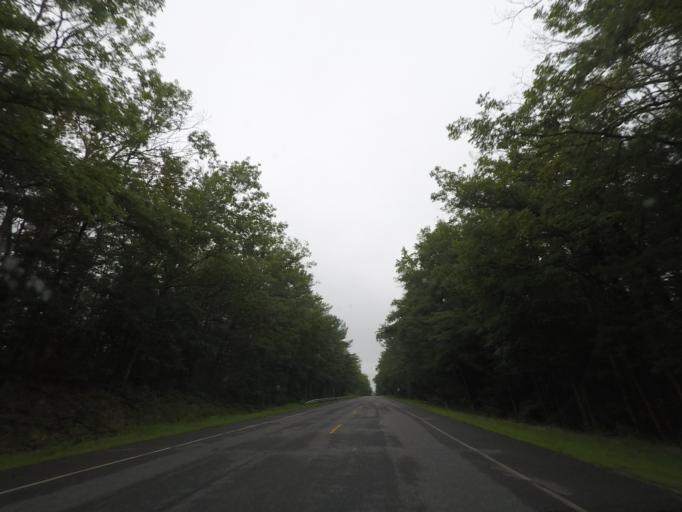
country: US
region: Massachusetts
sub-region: Worcester County
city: Sturbridge
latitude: 42.0844
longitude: -72.0909
